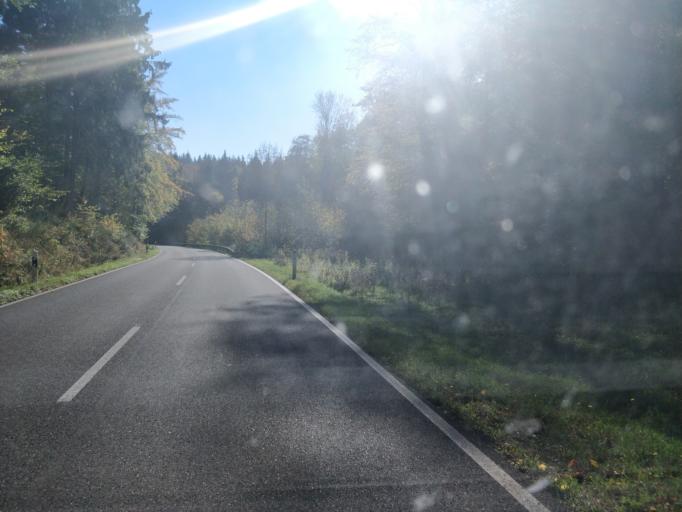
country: DE
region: North Rhine-Westphalia
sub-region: Regierungsbezirk Koln
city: Bad Munstereifel
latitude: 50.5537
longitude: 6.7988
